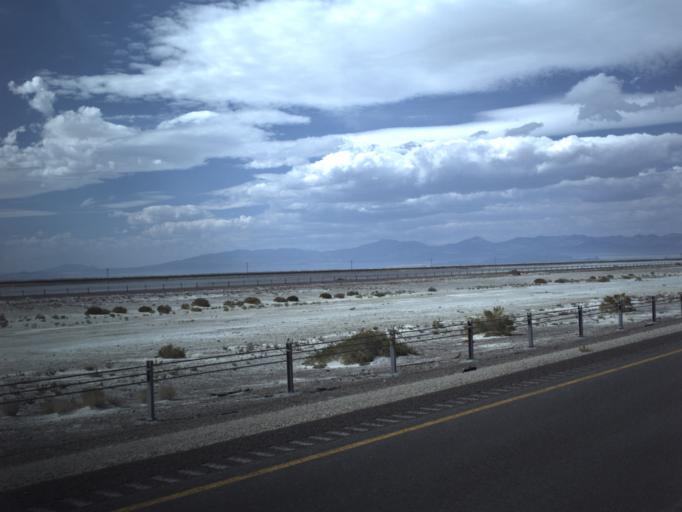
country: US
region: Utah
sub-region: Tooele County
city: Wendover
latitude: 40.7388
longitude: -113.8227
